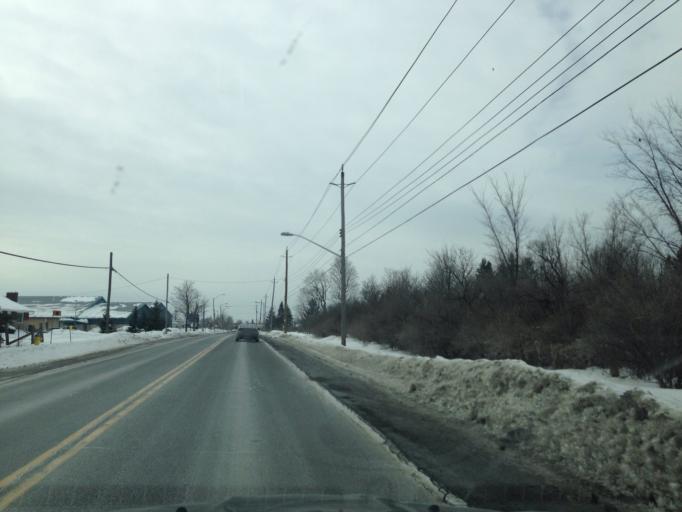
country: CA
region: Ontario
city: Ottawa
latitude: 45.3326
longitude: -75.5956
